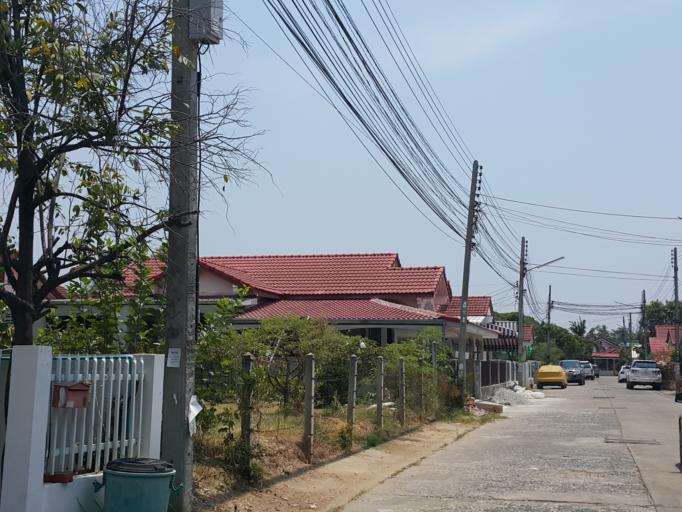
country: TH
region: Phitsanulok
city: Phitsanulok
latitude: 16.8189
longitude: 100.2475
